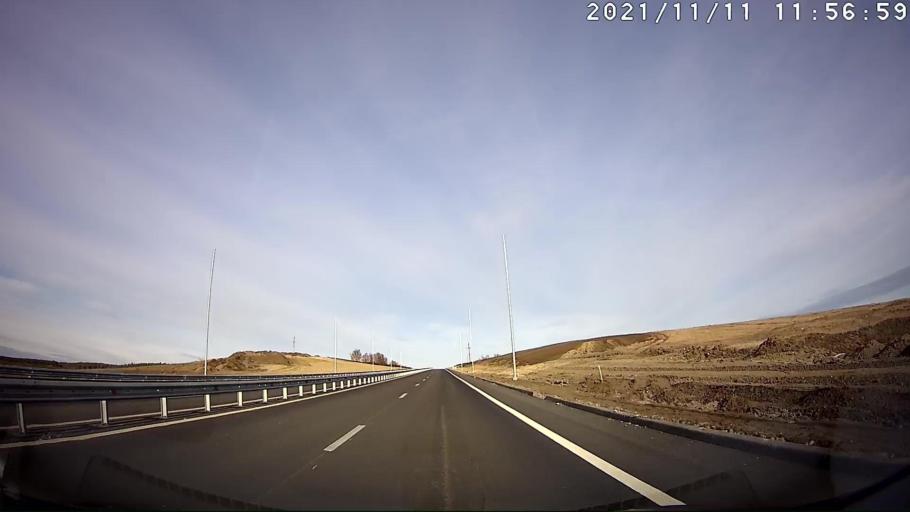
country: RU
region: Samara
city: Balasheyka
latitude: 53.5600
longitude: 48.3313
